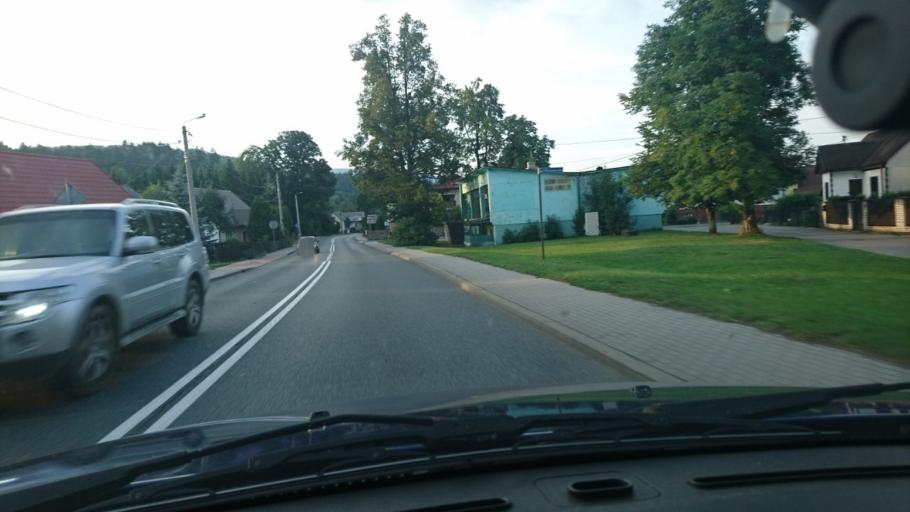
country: PL
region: Silesian Voivodeship
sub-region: Powiat zywiecki
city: Milowka
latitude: 49.5621
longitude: 19.0874
